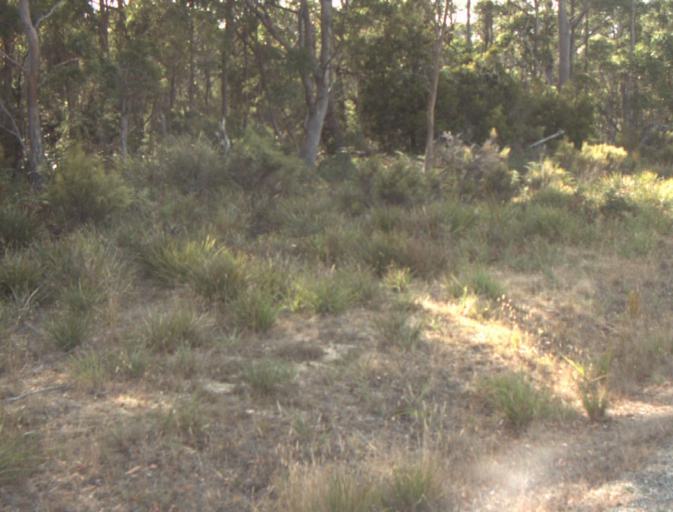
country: AU
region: Tasmania
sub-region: Dorset
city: Bridport
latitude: -41.1291
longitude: 147.2131
